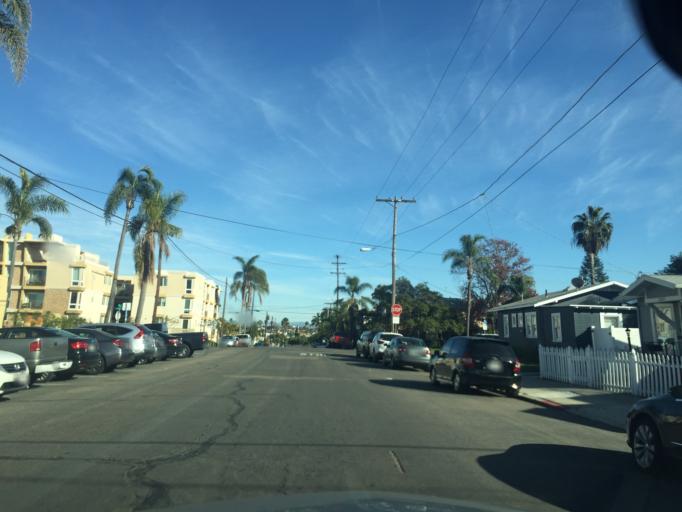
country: US
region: California
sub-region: San Diego County
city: San Diego
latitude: 32.7522
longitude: -117.1283
